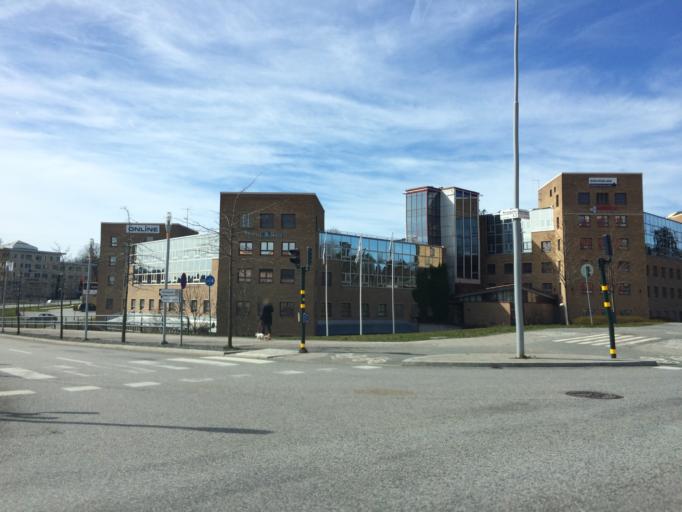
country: SE
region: Stockholm
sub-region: Stockholms Kommun
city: Kista
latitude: 59.4075
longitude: 17.9379
